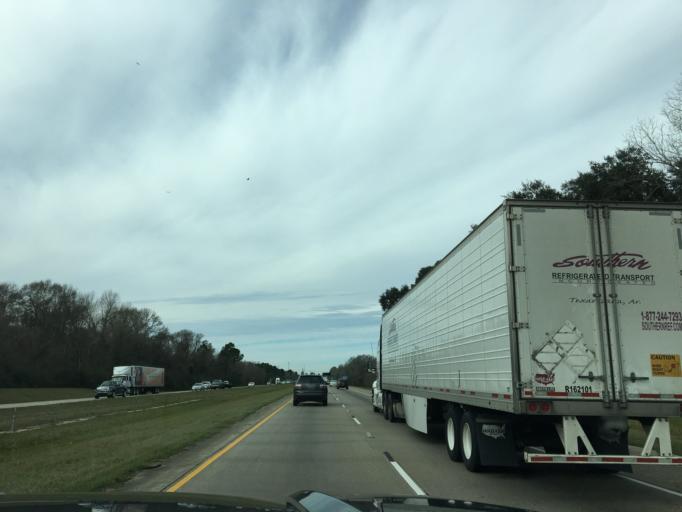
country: US
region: Louisiana
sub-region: Ascension Parish
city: Prairieville
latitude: 30.3272
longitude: -91.0108
